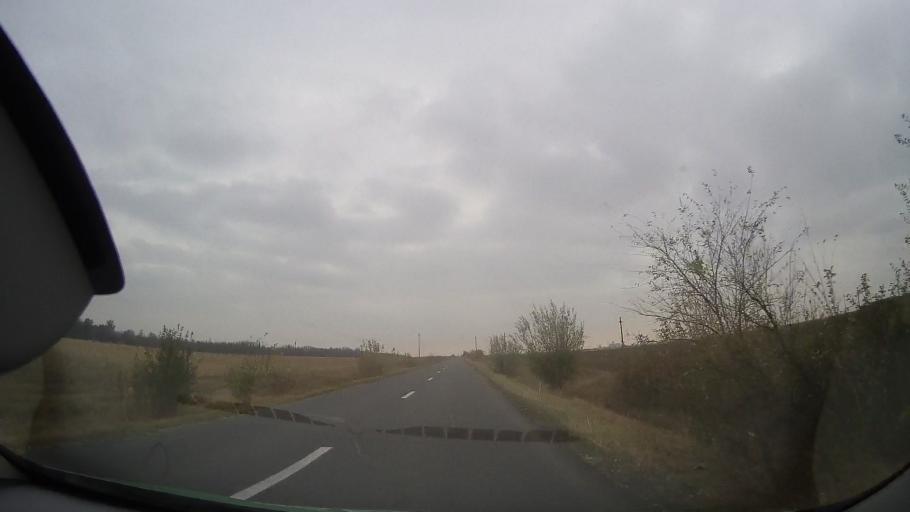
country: RO
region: Ialomita
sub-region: Comuna Manasia
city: Manasia
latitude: 44.7370
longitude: 26.7051
